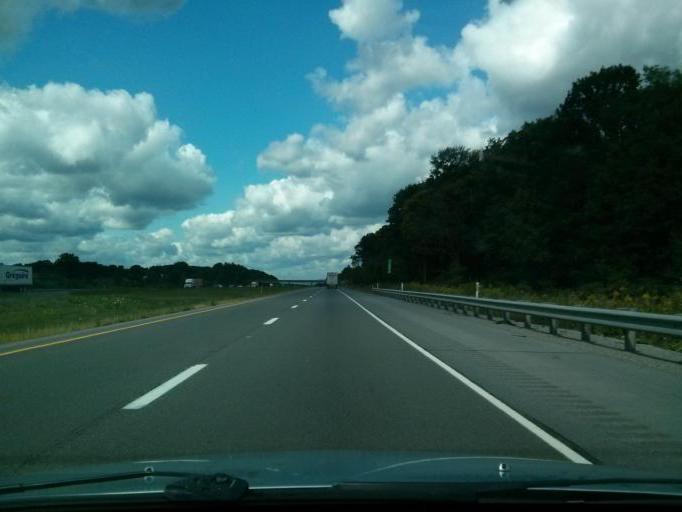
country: US
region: Pennsylvania
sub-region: Clearfield County
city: Treasure Lake
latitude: 41.1212
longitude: -78.6455
